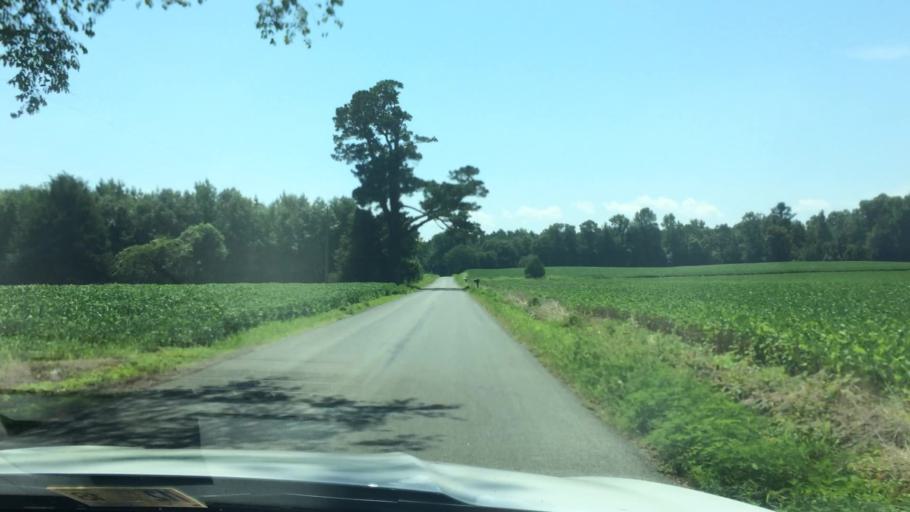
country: US
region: Virginia
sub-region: Charles City County
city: Charles City
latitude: 37.3059
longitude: -76.9654
